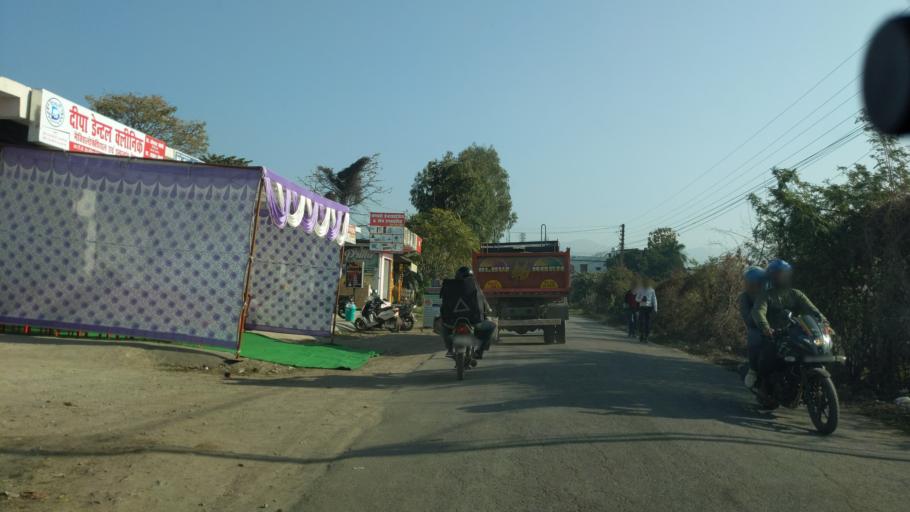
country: IN
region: Uttarakhand
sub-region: Naini Tal
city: Haldwani
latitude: 29.2110
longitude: 79.4914
